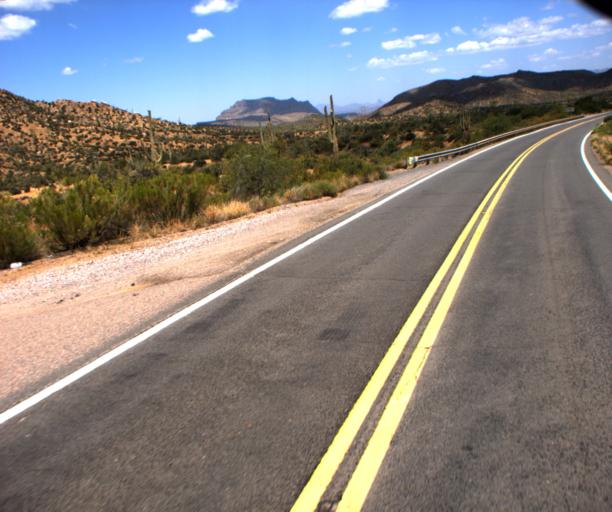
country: US
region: Arizona
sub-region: Pinal County
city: Superior
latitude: 33.2150
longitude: -111.0648
